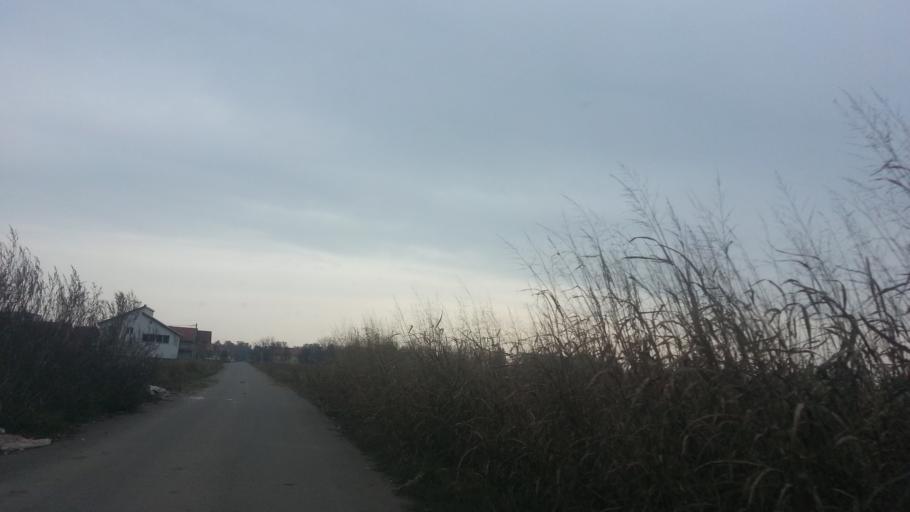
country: RS
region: Autonomna Pokrajina Vojvodina
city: Nova Pazova
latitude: 44.9578
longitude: 20.2054
